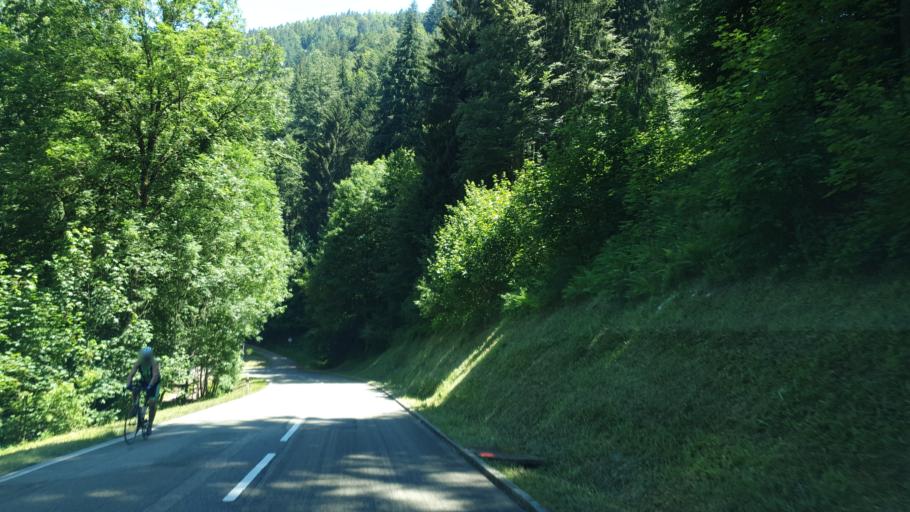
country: DE
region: Baden-Wuerttemberg
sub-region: Freiburg Region
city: Horben
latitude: 47.9252
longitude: 7.8760
